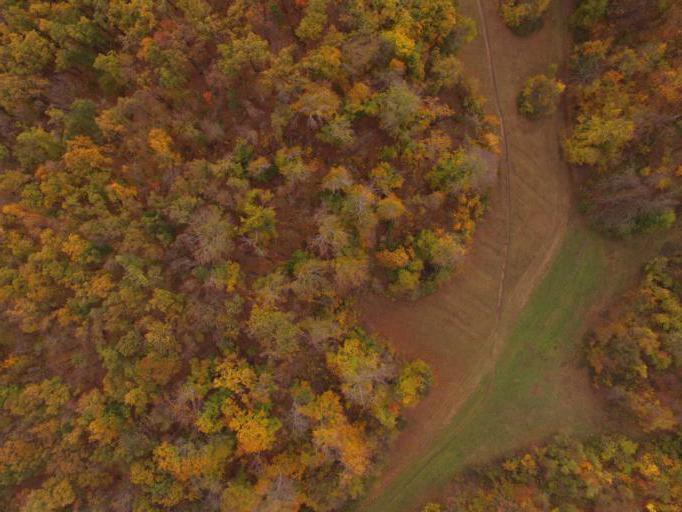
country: HU
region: Pest
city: Budakeszi
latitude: 47.5070
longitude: 18.9695
